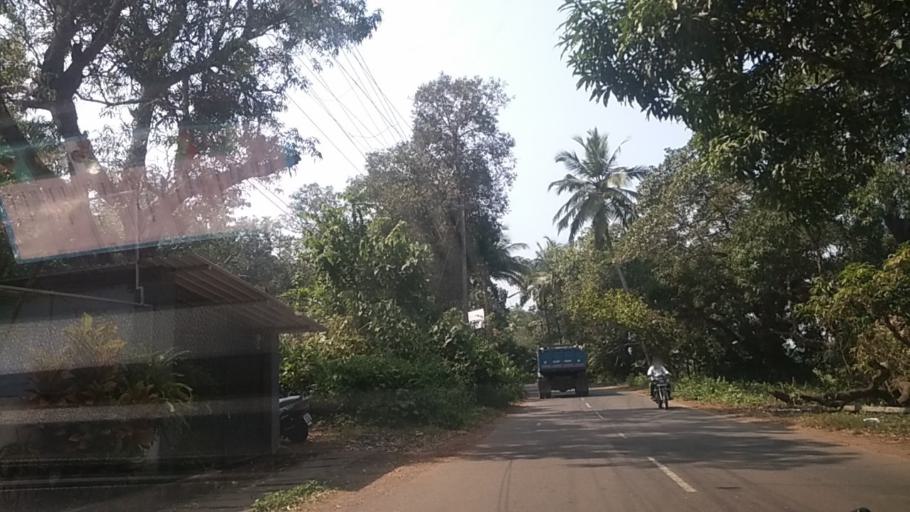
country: IN
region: Goa
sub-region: North Goa
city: Solim
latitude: 15.6158
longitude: 73.7832
